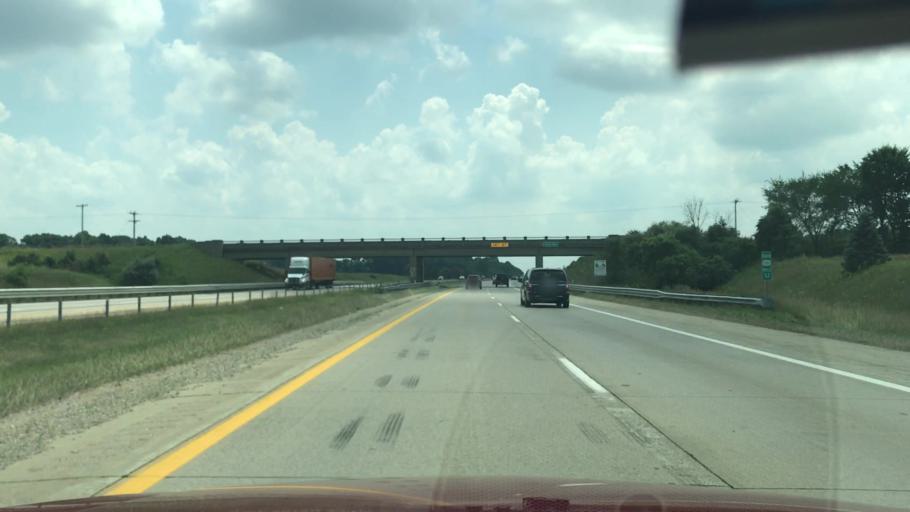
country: US
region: Michigan
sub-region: Allegan County
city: Plainwell
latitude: 42.4946
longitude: -85.6520
